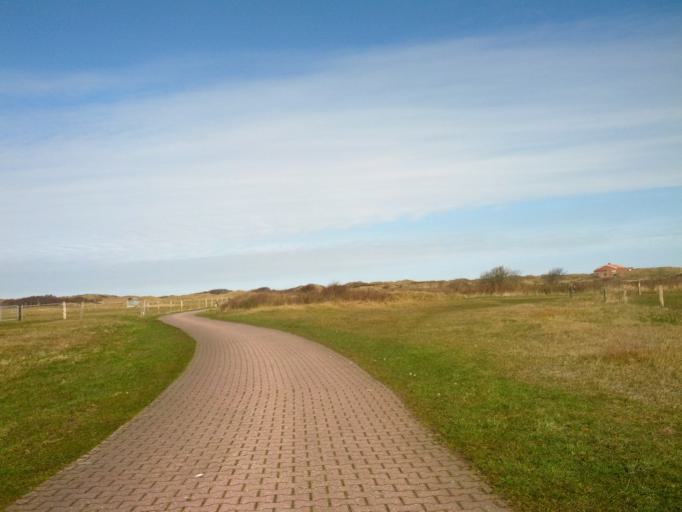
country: DE
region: Lower Saxony
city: Langeoog
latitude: 53.7474
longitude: 7.5030
